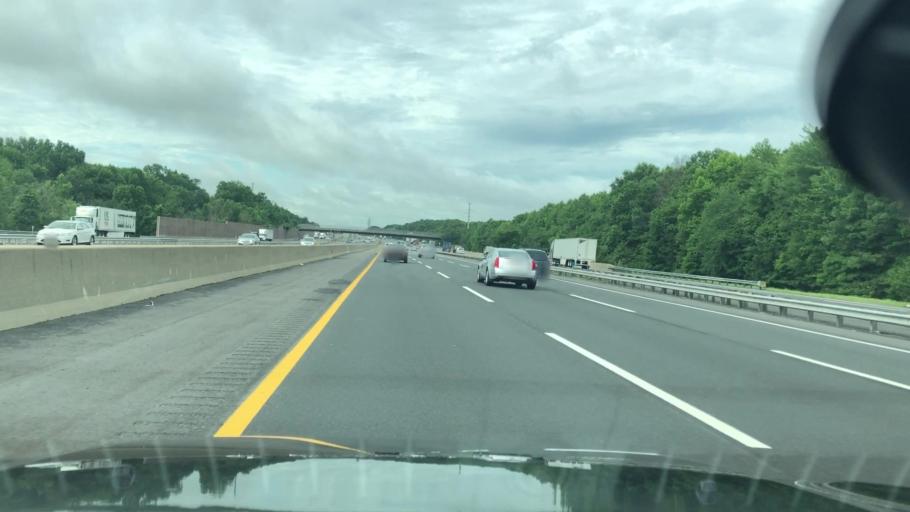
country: US
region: New Jersey
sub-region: Middlesex County
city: East Brunswick
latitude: 40.4304
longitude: -74.4378
